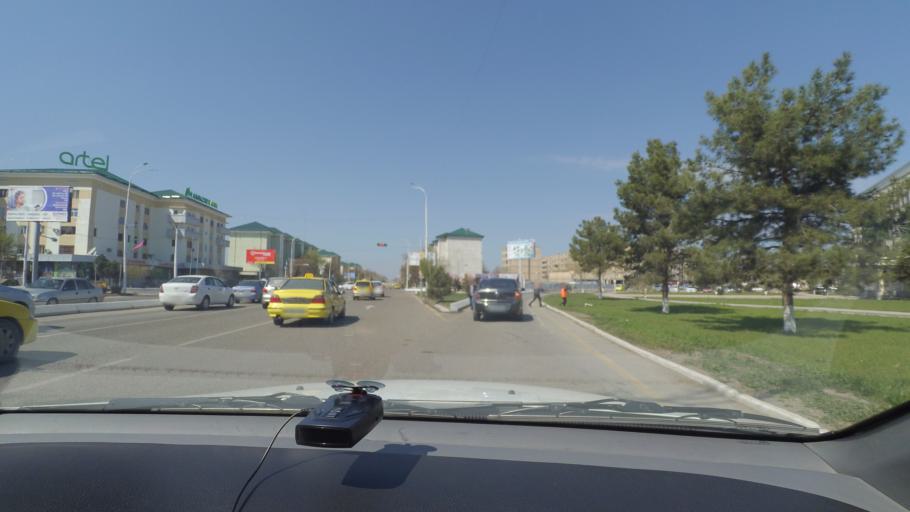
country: UZ
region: Bukhara
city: Bukhara
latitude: 39.7697
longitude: 64.4511
